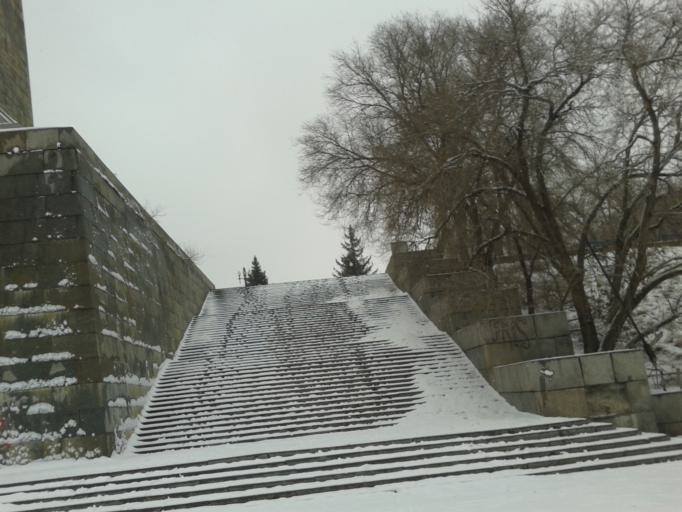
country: RU
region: Volgograd
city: Krasnoslobodsk
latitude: 48.5279
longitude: 44.5586
